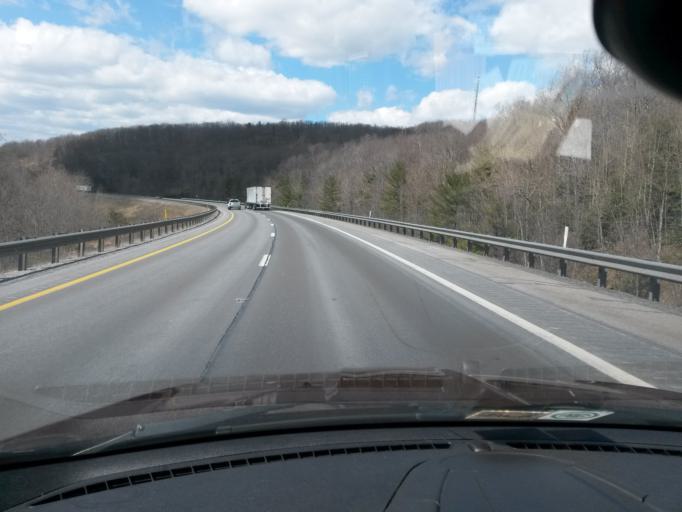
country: US
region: West Virginia
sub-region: Raleigh County
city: Shady Spring
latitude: 37.6944
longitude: -81.1297
